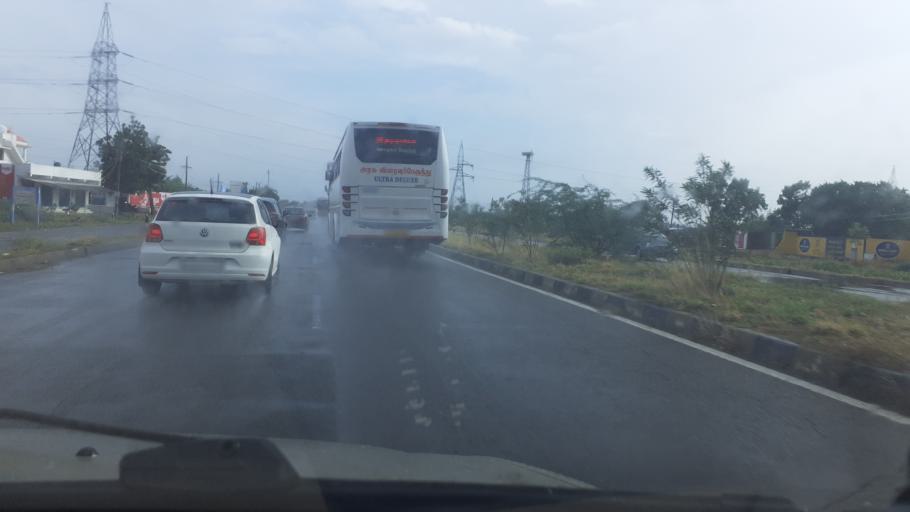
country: IN
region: Tamil Nadu
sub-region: Tirunelveli Kattabo
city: Gangaikondan
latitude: 8.8871
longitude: 77.7687
